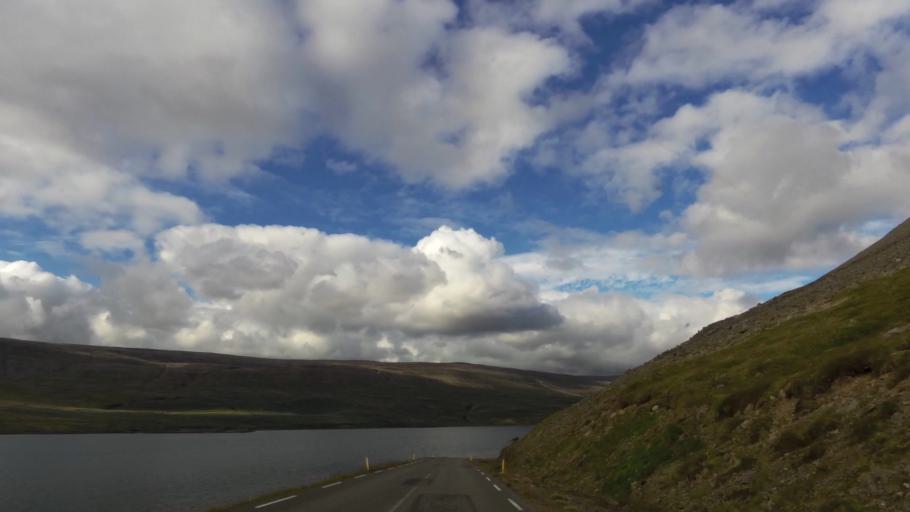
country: IS
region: West
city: Olafsvik
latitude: 65.5244
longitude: -23.8248
